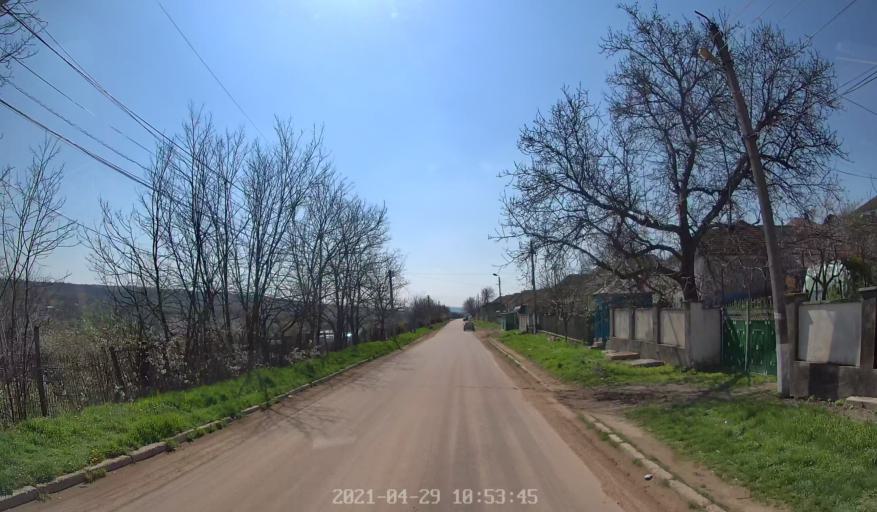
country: MD
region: Chisinau
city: Ciorescu
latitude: 47.1638
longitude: 28.9508
